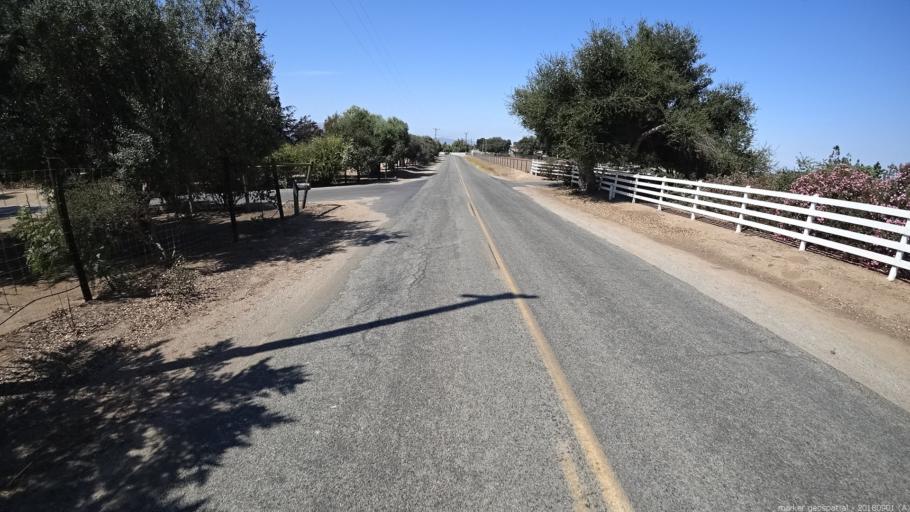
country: US
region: California
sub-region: Monterey County
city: Chualar
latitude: 36.5904
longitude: -121.4558
